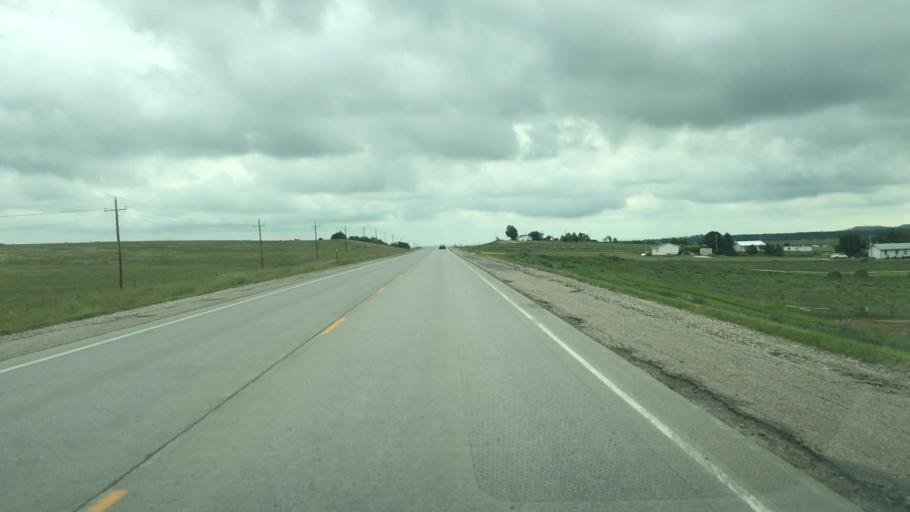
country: US
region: South Dakota
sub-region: Todd County
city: Mission
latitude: 43.3029
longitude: -100.7015
